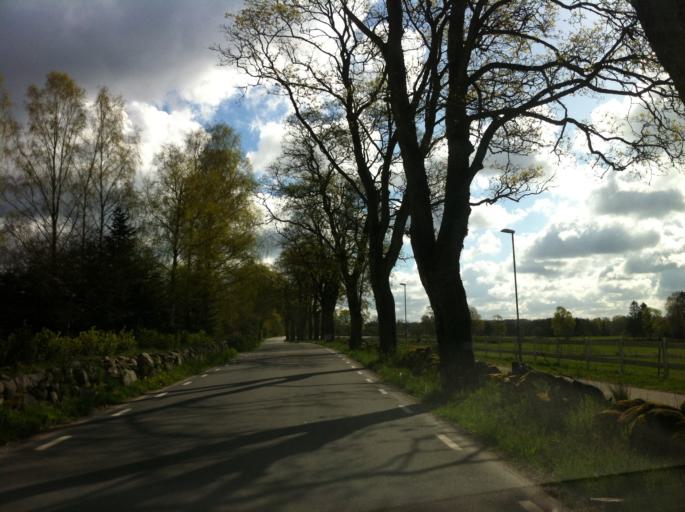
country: SE
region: Skane
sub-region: Hoors Kommun
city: Satofta
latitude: 55.9080
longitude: 13.5682
